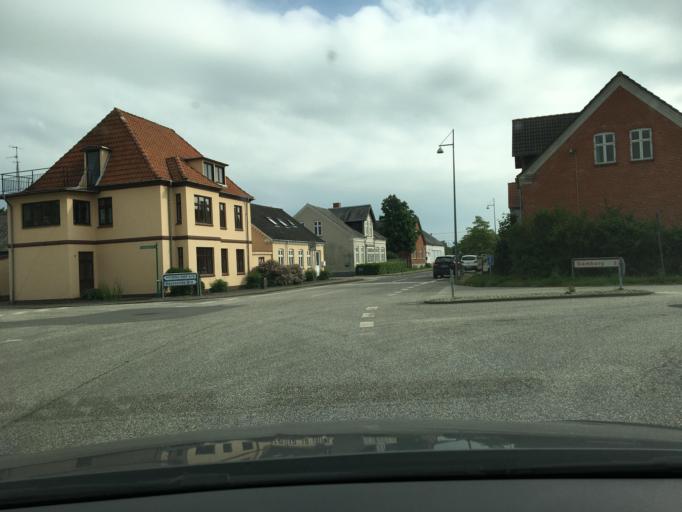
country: DK
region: South Denmark
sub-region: Middelfart Kommune
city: Norre Aby
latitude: 55.4775
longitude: 9.8105
